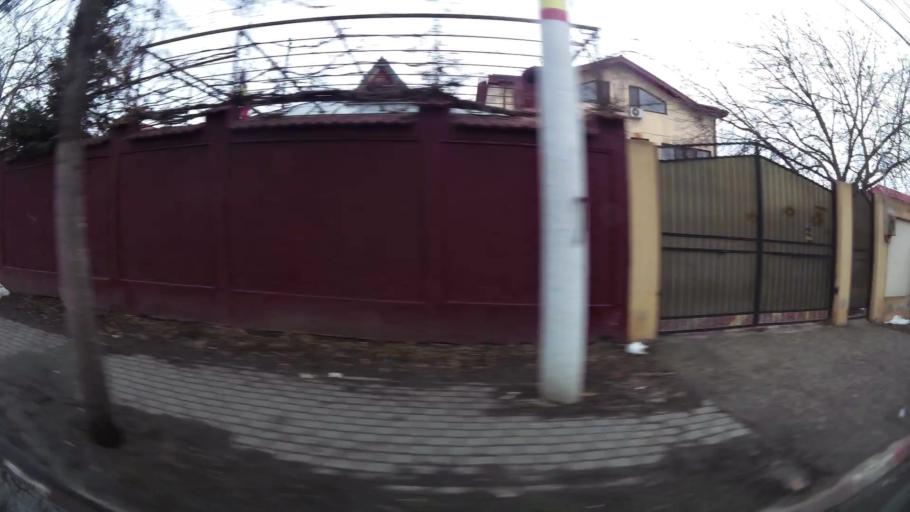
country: RO
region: Ilfov
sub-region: Voluntari City
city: Voluntari
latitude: 44.4955
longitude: 26.1896
